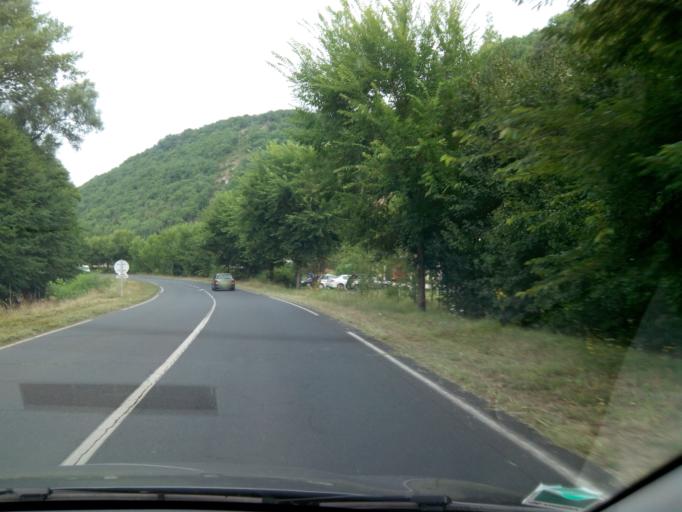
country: FR
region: Midi-Pyrenees
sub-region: Departement du Lot
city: Souillac
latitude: 44.8885
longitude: 1.4039
